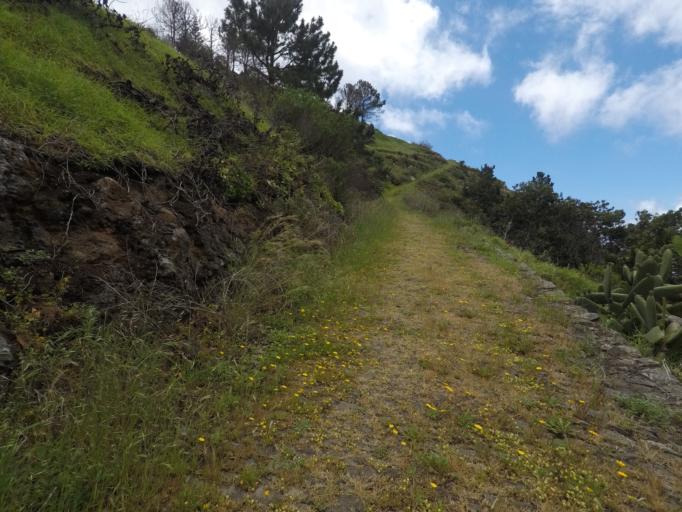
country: PT
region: Madeira
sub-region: Calheta
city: Faja da Ovelha
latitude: 32.7536
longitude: -17.2177
